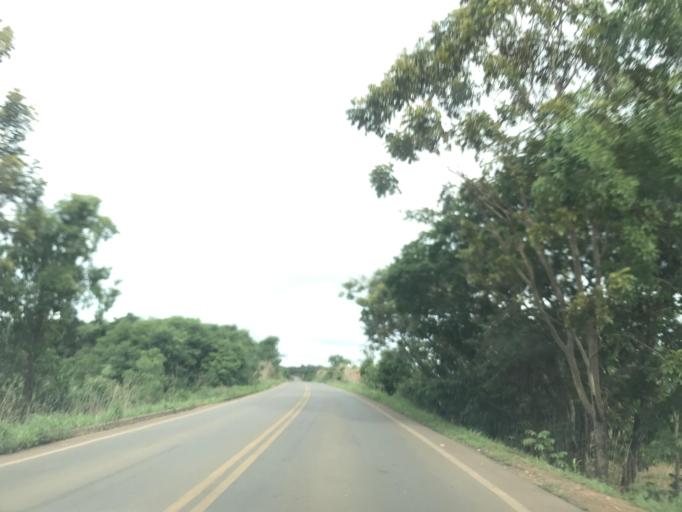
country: BR
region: Goias
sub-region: Vianopolis
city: Vianopolis
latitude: -16.7254
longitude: -48.4226
